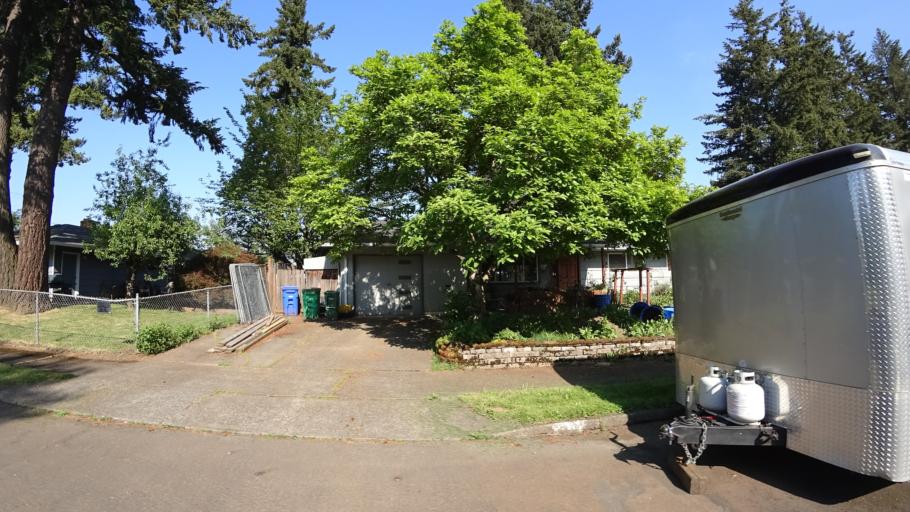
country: US
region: Oregon
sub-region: Multnomah County
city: Lents
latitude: 45.5098
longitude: -122.5086
